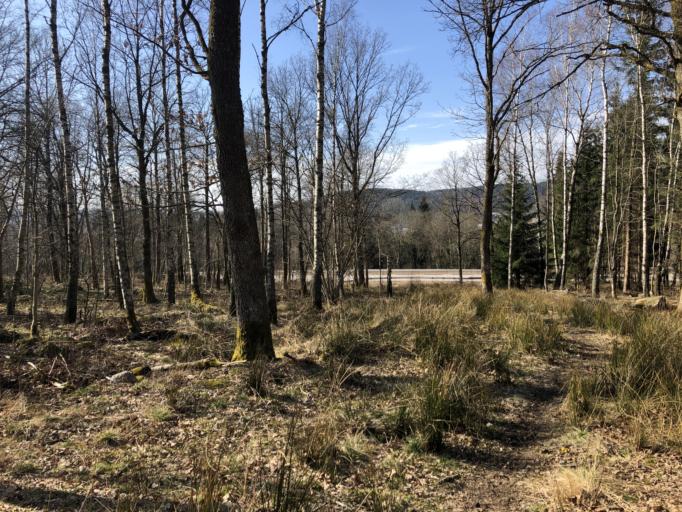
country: SE
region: Vaestra Goetaland
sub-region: Ulricehamns Kommun
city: Ulricehamn
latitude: 57.8063
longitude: 13.4287
